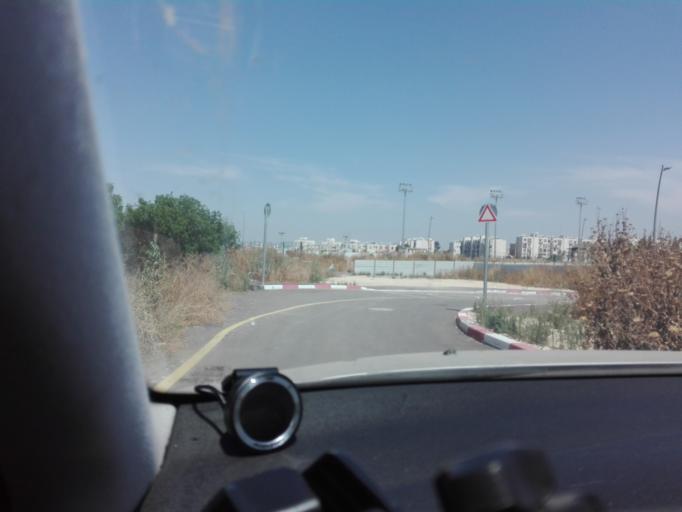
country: IL
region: Central District
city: Bene 'Ayish
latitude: 31.7347
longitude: 34.7360
